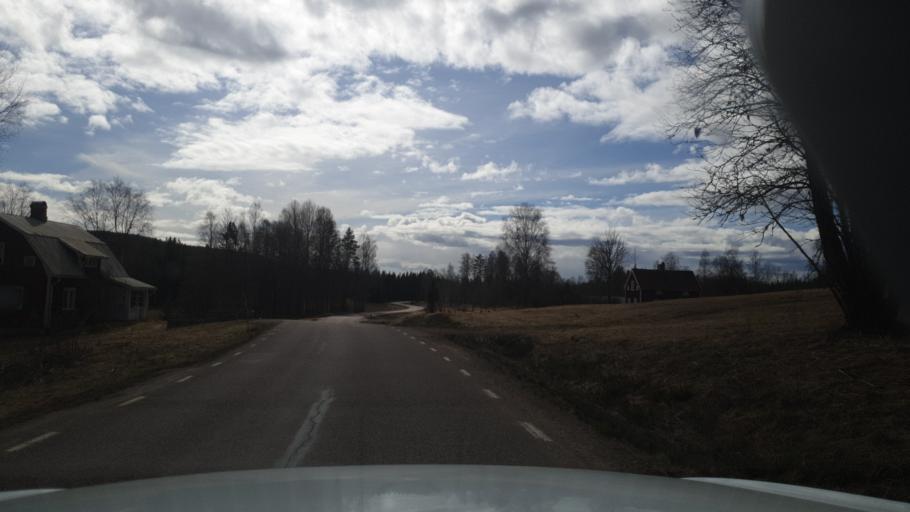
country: SE
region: Vaermland
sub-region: Arvika Kommun
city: Arvika
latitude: 59.7608
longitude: 12.8220
